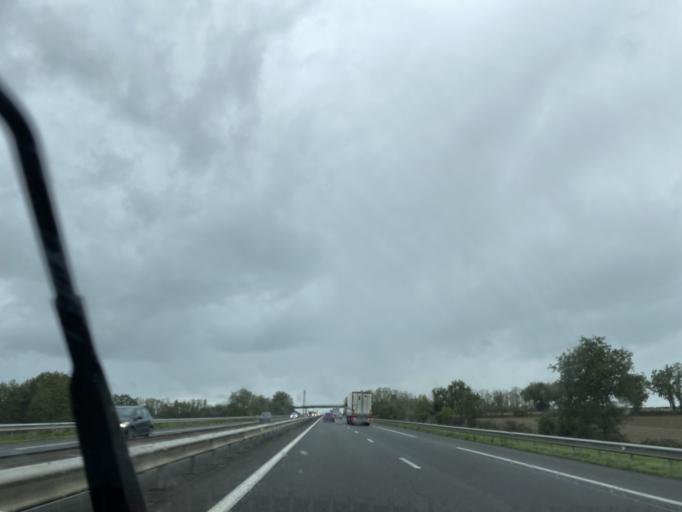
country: FR
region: Auvergne
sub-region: Departement de l'Allier
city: Doyet
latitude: 46.3680
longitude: 2.7424
